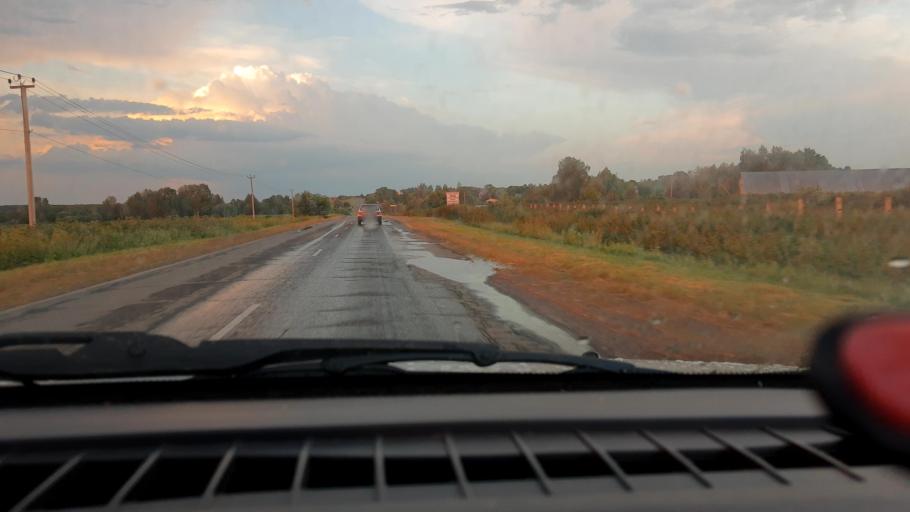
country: RU
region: Nizjnij Novgorod
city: Afonino
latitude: 56.1289
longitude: 44.0118
